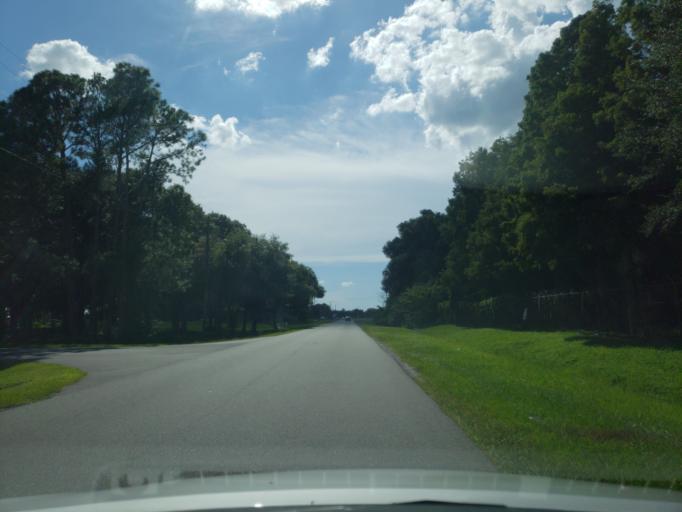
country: US
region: Florida
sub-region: Hillsborough County
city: Egypt Lake-Leto
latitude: 27.9940
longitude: -82.5192
